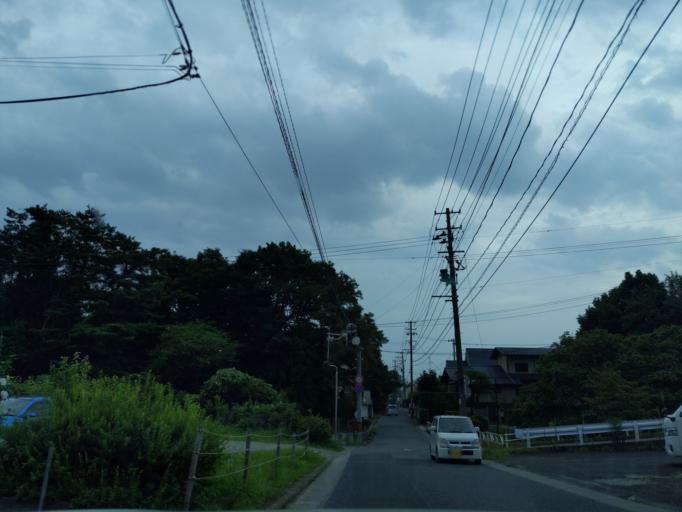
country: JP
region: Fukushima
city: Koriyama
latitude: 37.3814
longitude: 140.3566
